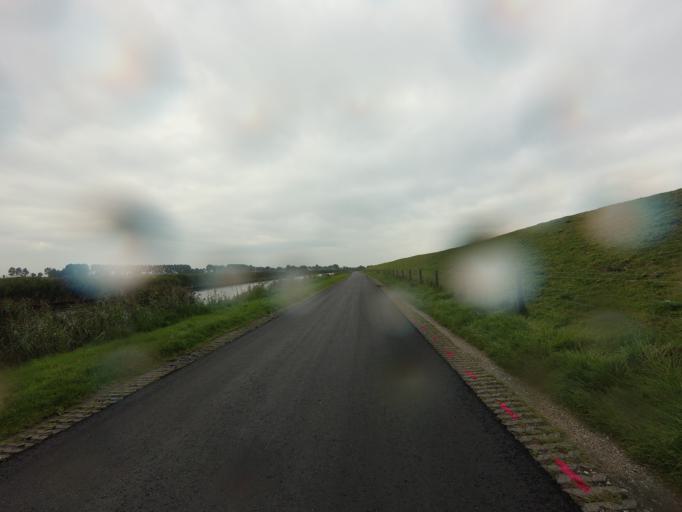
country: NL
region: Friesland
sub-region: Sudwest Fryslan
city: Koudum
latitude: 52.9081
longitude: 5.4047
